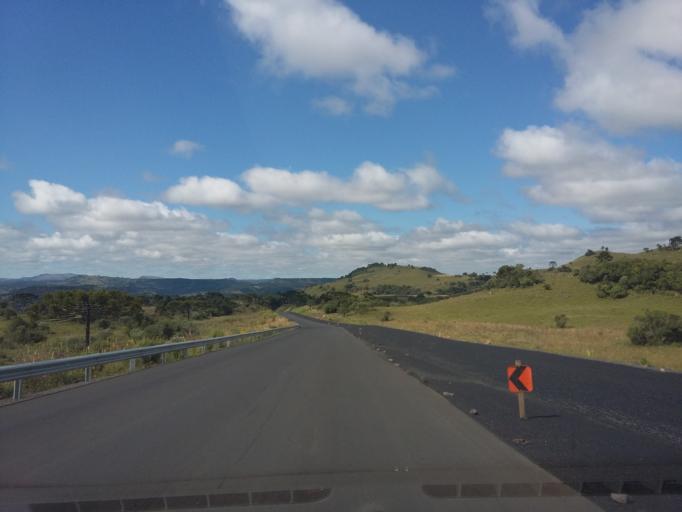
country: BR
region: Santa Catarina
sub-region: Sao Joaquim
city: Sao Joaquim
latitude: -28.0691
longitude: -50.0733
